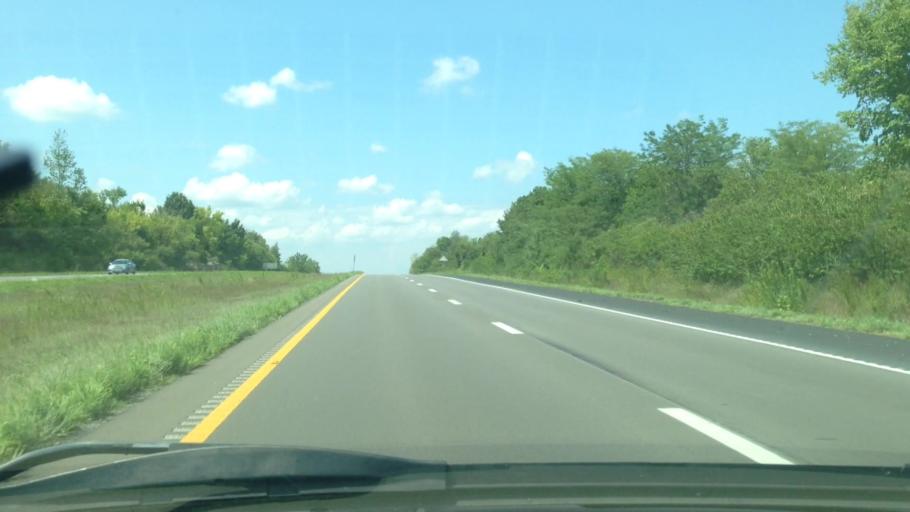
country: US
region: Missouri
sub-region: Lincoln County
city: Troy
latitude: 38.9962
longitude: -90.9690
